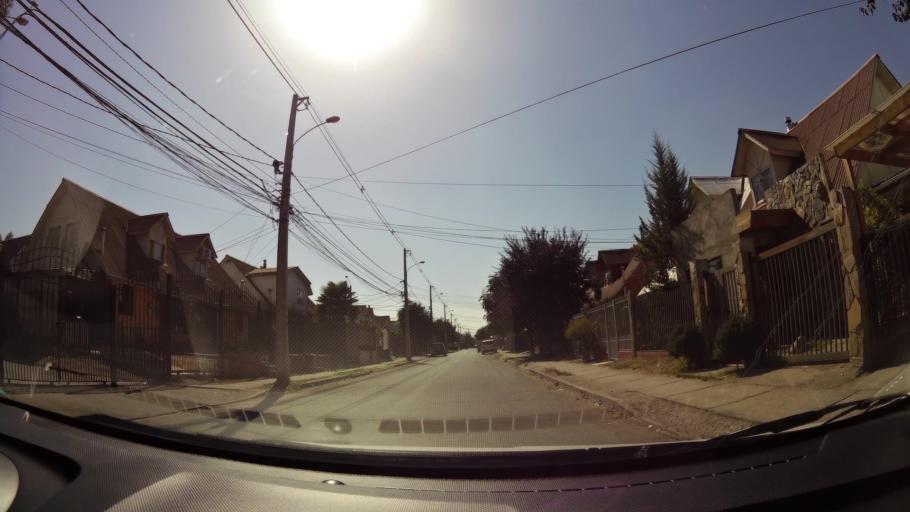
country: CL
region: Maule
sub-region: Provincia de Talca
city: Talca
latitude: -35.4091
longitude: -71.6424
